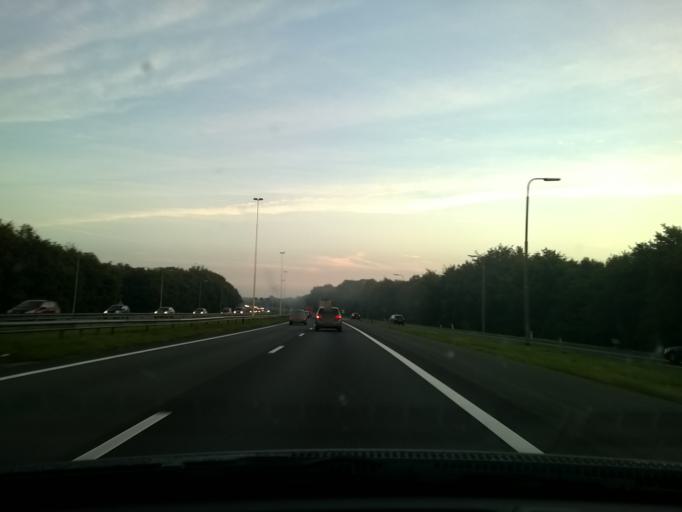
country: NL
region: North Holland
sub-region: Gemeente Laren
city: Laren
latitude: 52.2360
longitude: 5.2434
